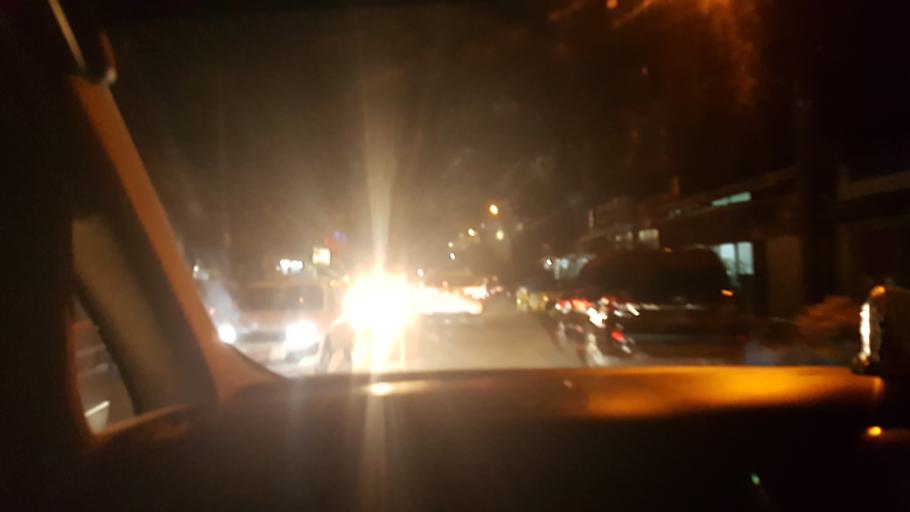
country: MM
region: Yangon
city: Yangon
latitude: 16.8192
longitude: 96.1289
